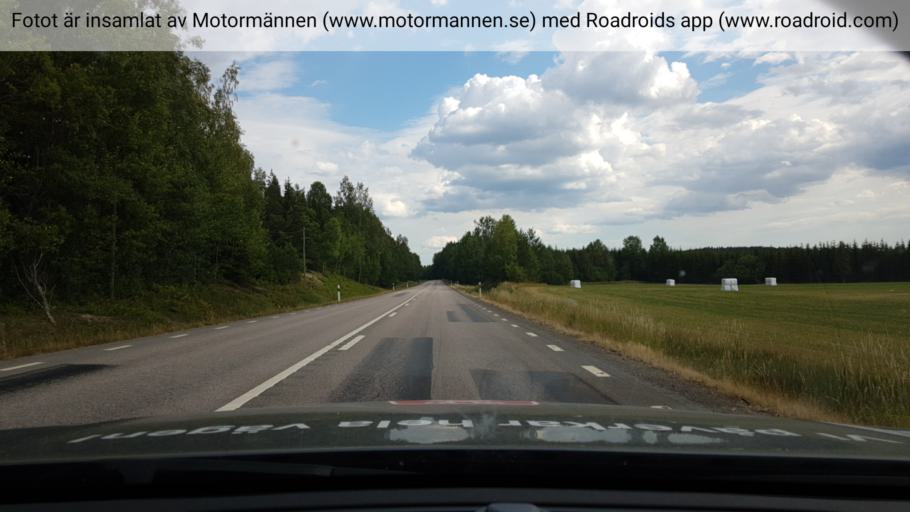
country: SE
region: Uppsala
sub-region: Heby Kommun
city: Morgongava
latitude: 59.9159
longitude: 17.0250
